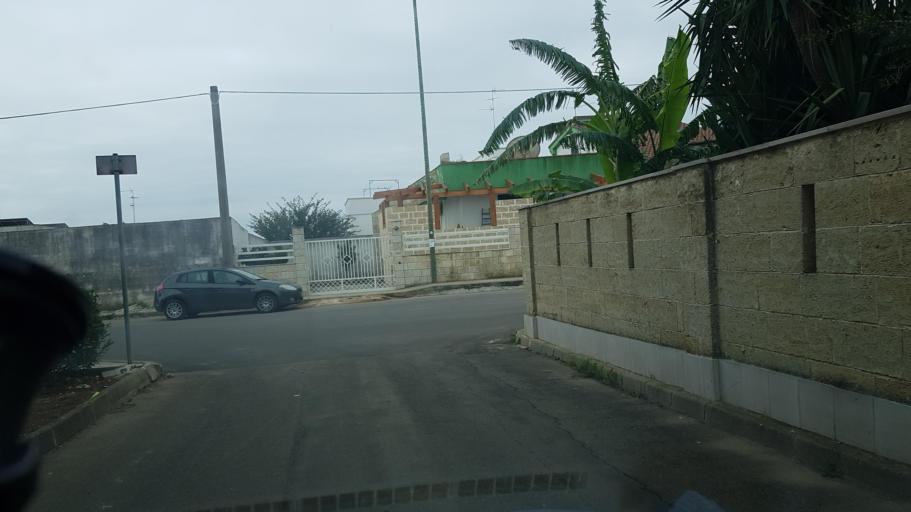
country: IT
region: Apulia
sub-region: Provincia di Lecce
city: Veglie
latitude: 40.3390
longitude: 17.9518
